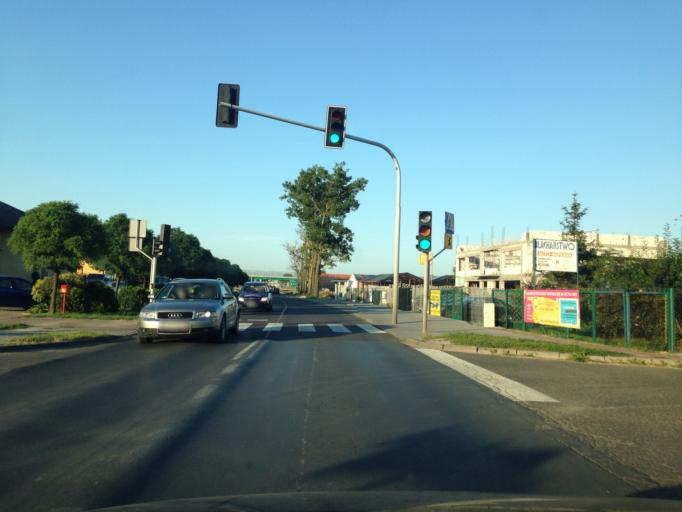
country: PL
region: Kujawsko-Pomorskie
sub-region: Powiat aleksandrowski
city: Ciechocinek
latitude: 52.8686
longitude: 18.7475
